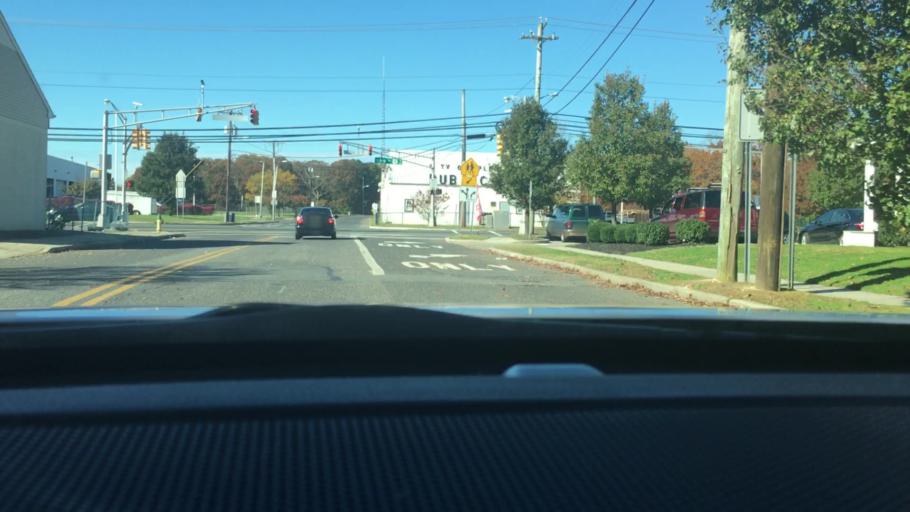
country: US
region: New Jersey
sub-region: Atlantic County
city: Pleasantville
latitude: 39.4050
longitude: -74.5217
